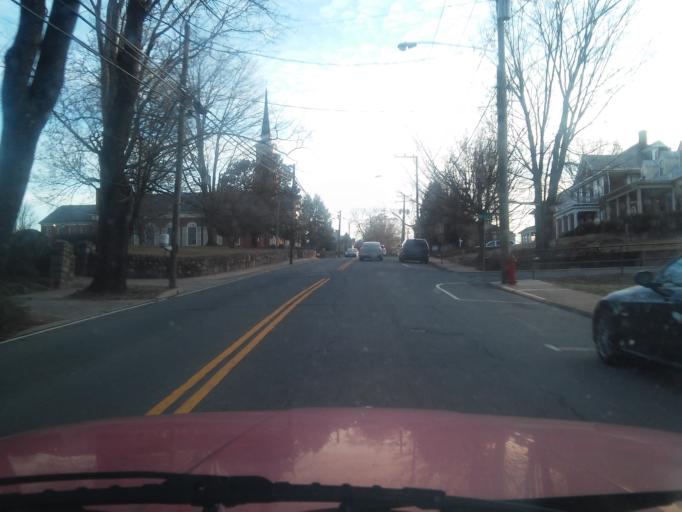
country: US
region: Virginia
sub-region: City of Charlottesville
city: Charlottesville
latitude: 38.0346
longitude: -78.4758
